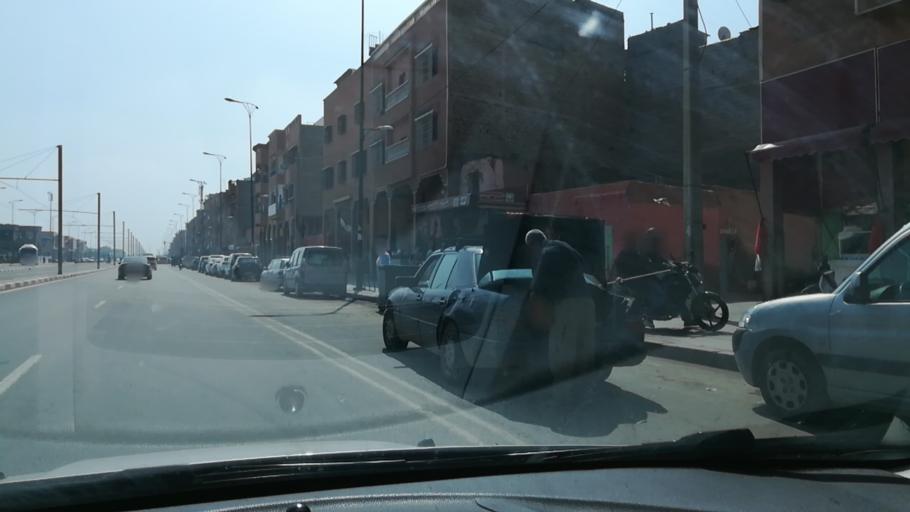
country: MA
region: Marrakech-Tensift-Al Haouz
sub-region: Marrakech
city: Marrakesh
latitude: 31.6278
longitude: -8.0652
